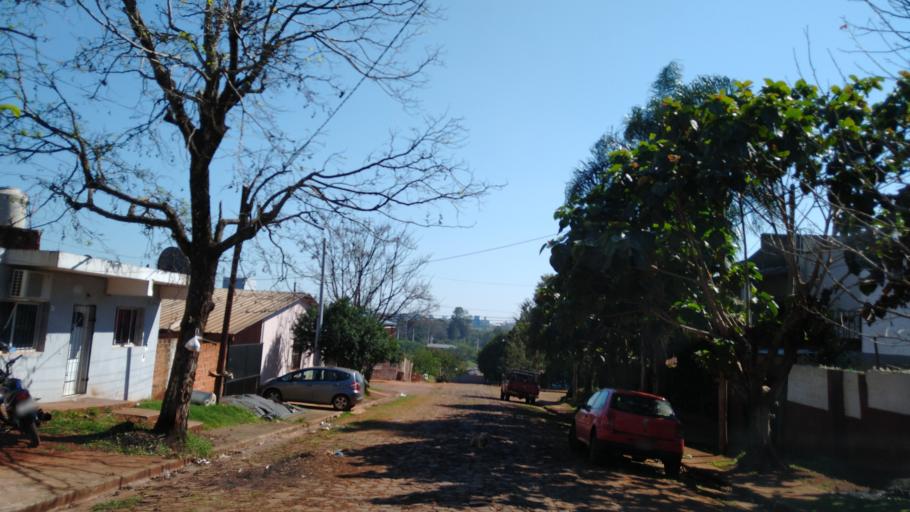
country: AR
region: Misiones
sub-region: Departamento de Capital
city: Posadas
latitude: -27.3991
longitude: -55.9421
